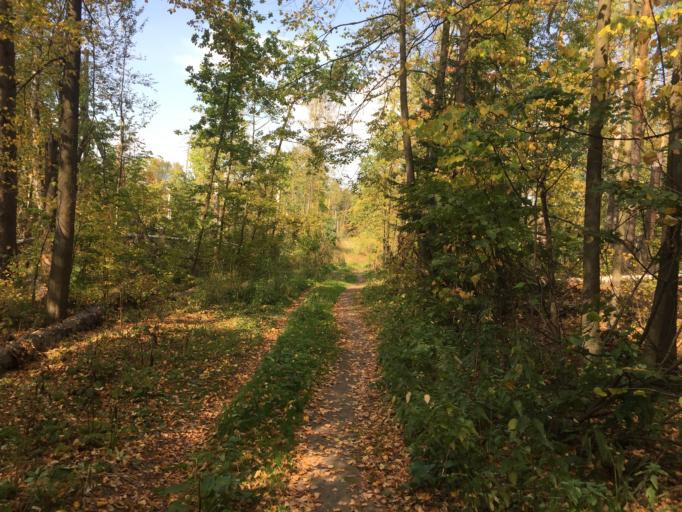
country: RU
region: Moscow
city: Babushkin
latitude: 55.8440
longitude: 37.7443
